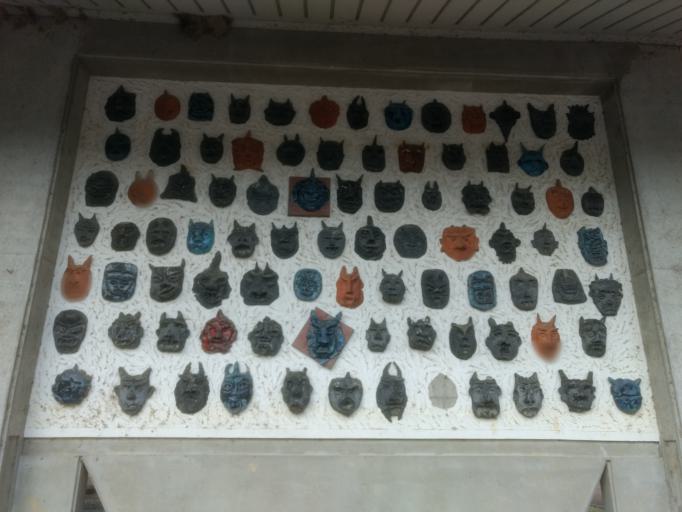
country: JP
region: Kyoto
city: Fukuchiyama
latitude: 35.3889
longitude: 135.1470
